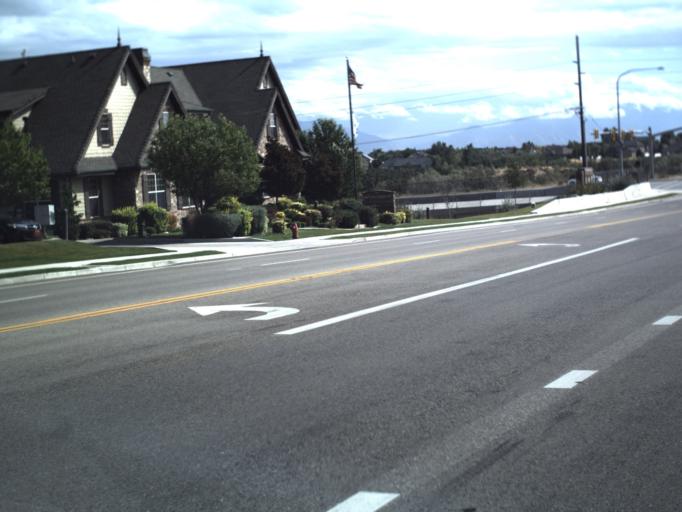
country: US
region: Utah
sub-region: Utah County
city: Alpine
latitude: 40.4331
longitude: -111.8221
